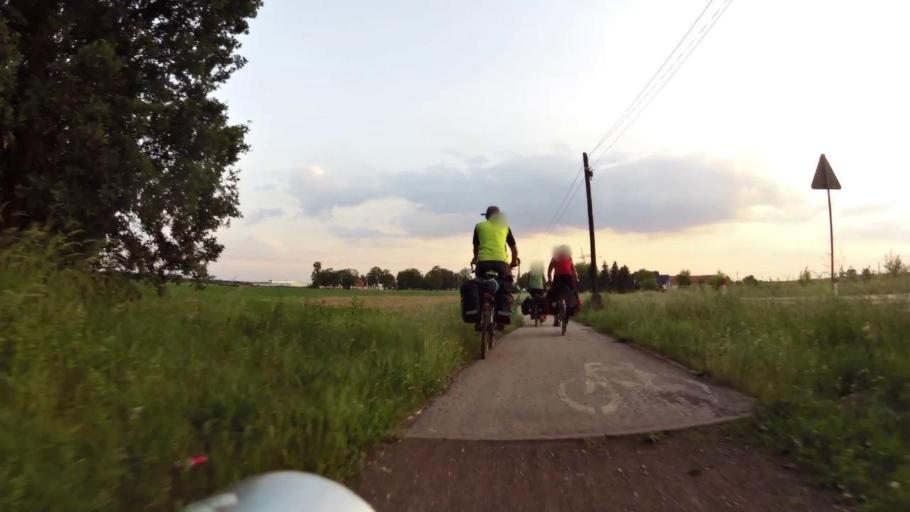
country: PL
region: Kujawsko-Pomorskie
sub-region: Powiat bydgoski
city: Dabrowa Chelminska
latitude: 53.1596
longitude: 18.2401
